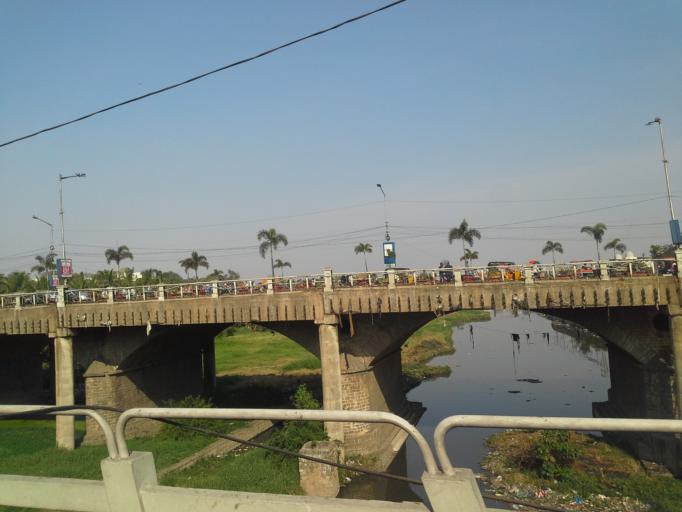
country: IN
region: Telangana
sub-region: Hyderabad
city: Hyderabad
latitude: 17.3710
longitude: 78.4763
